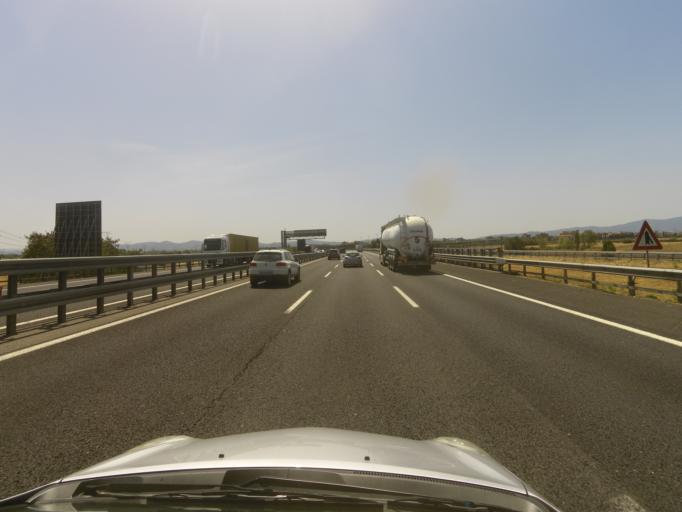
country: IT
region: Tuscany
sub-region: Province of Florence
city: Campi Bisenzio
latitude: 43.8297
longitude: 11.1542
